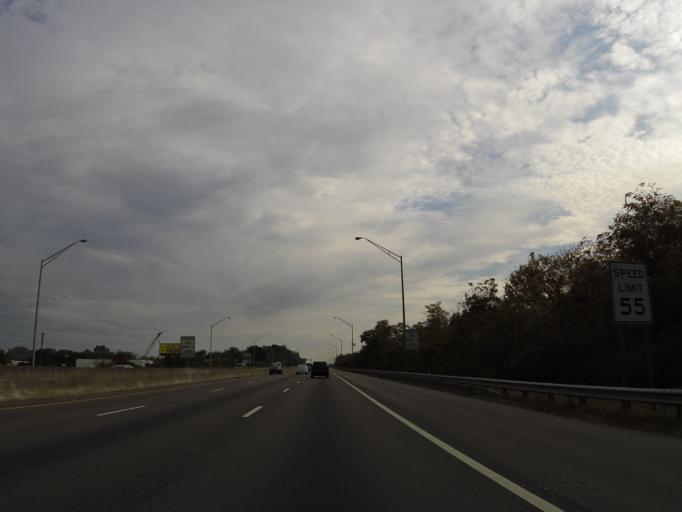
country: US
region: Tennessee
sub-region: Knox County
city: Knoxville
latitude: 35.9949
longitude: -83.8963
